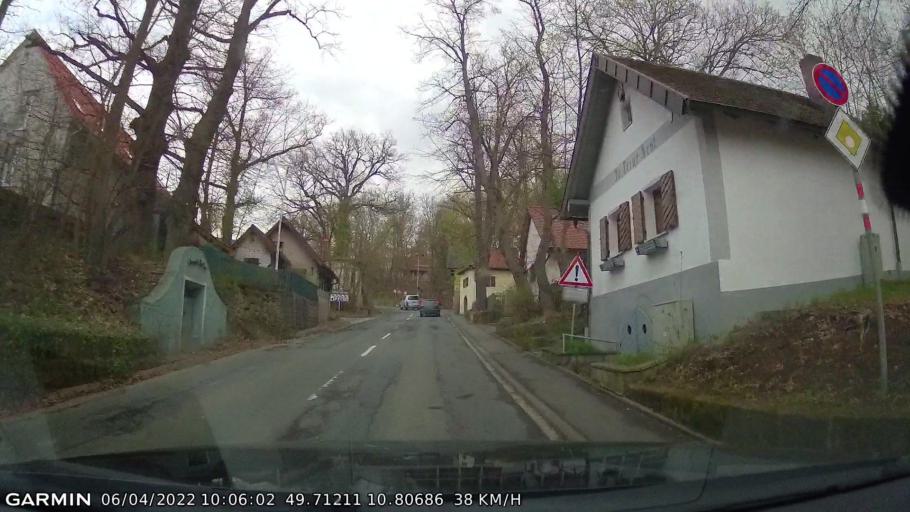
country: DE
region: Bavaria
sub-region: Regierungsbezirk Mittelfranken
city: Hochstadt an der Aisch
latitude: 49.7122
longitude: 10.8069
